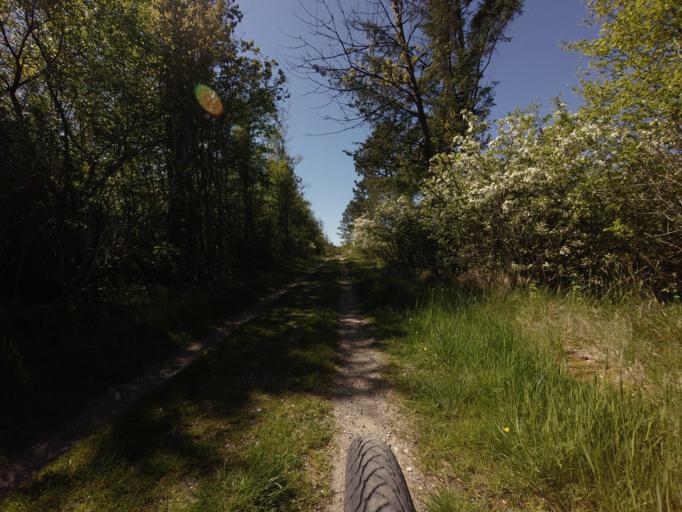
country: DK
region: North Denmark
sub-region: Jammerbugt Kommune
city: Pandrup
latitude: 57.2734
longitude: 9.6300
